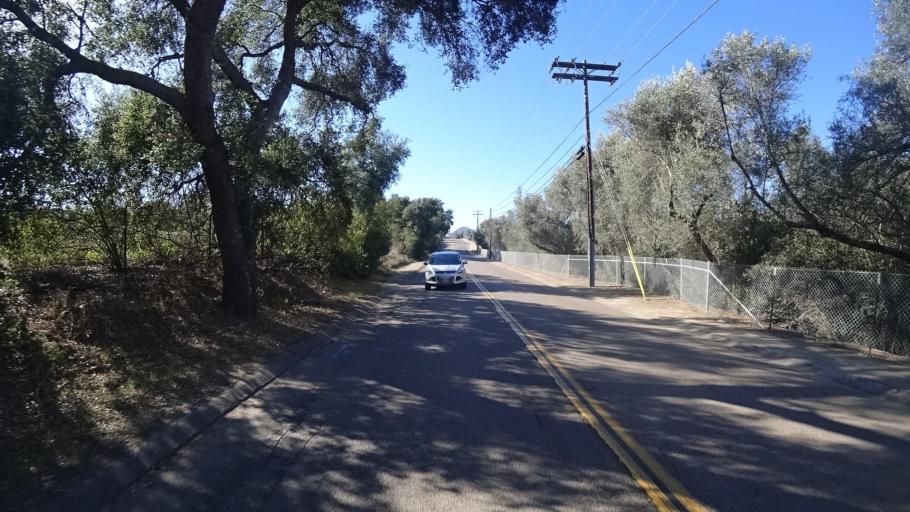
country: US
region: California
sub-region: San Diego County
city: Jamul
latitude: 32.7213
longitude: -116.8753
